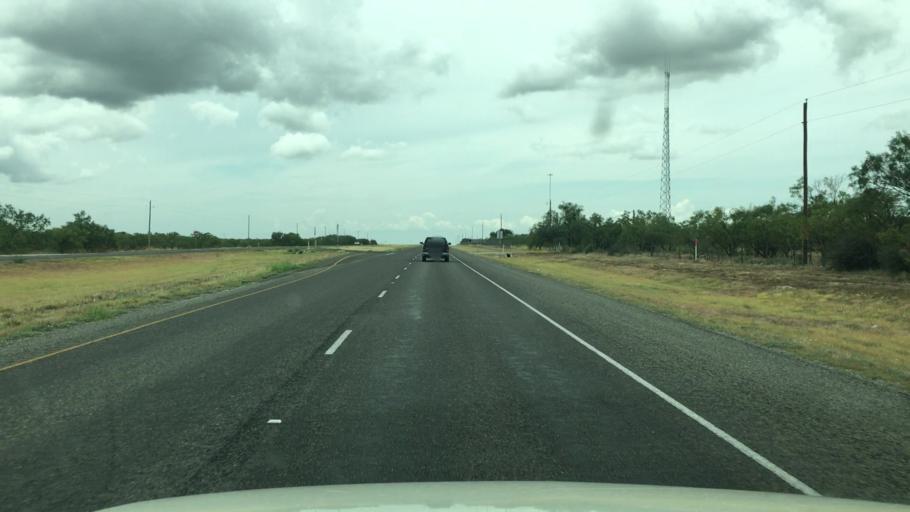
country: US
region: Texas
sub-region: Concho County
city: Eden
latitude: 31.2215
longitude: -99.9701
